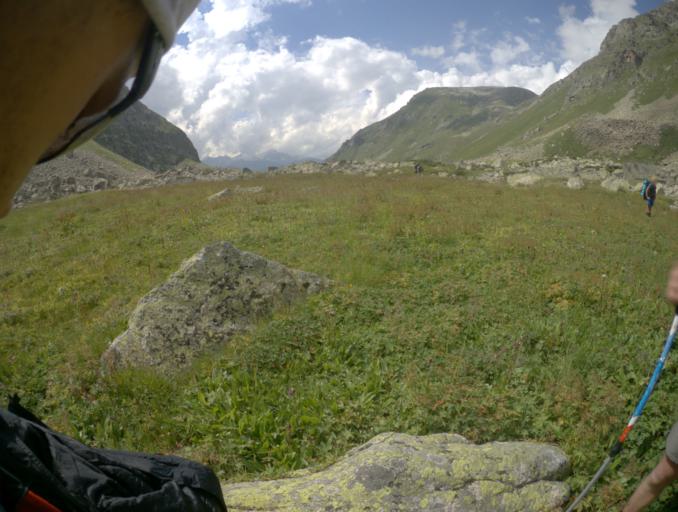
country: RU
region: Karachayevo-Cherkesiya
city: Uchkulan
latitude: 43.2865
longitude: 42.0859
